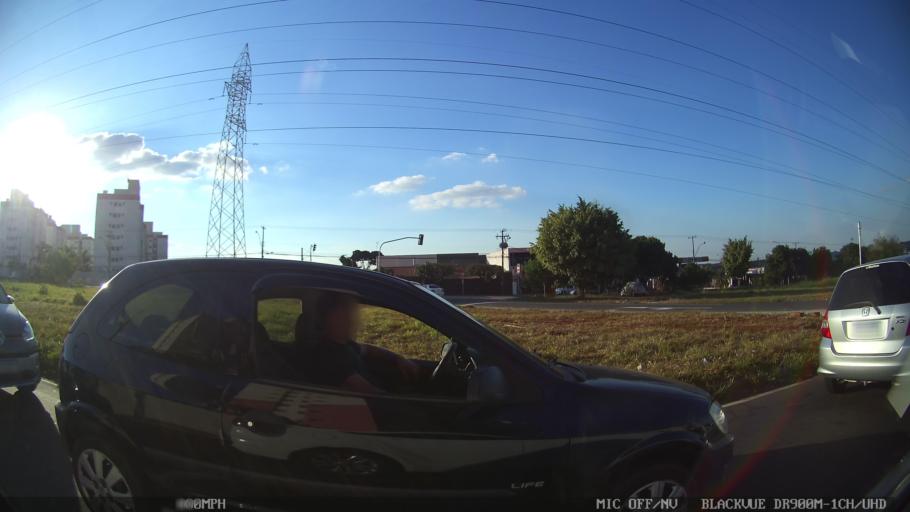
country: BR
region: Sao Paulo
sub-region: Americana
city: Americana
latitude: -22.7226
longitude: -47.3345
